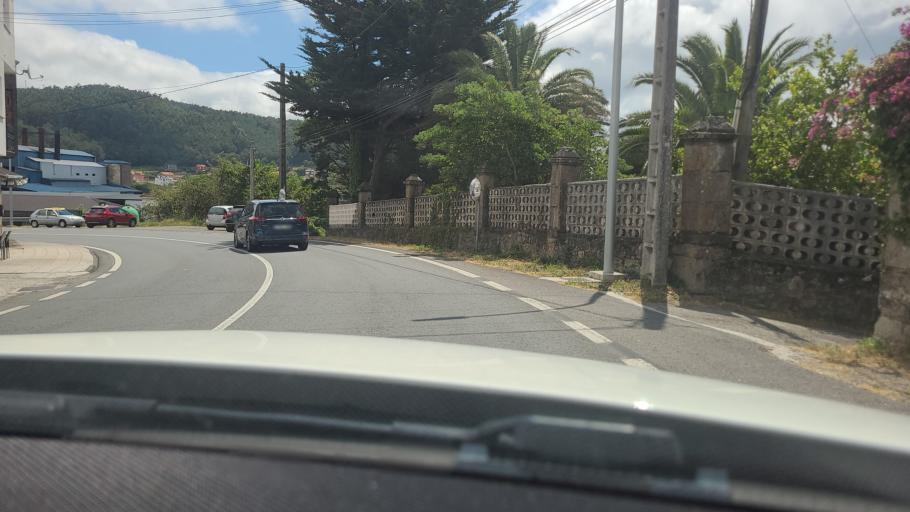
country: ES
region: Galicia
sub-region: Provincia da Coruna
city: Cee
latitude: 42.9466
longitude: -9.1794
